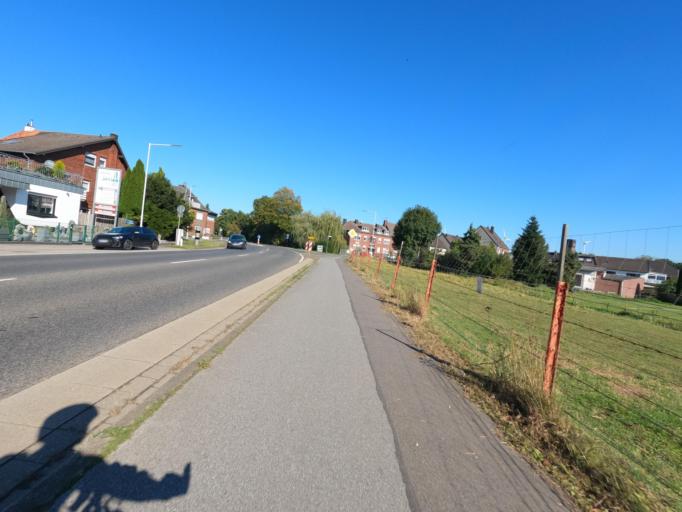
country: DE
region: North Rhine-Westphalia
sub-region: Regierungsbezirk Koln
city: Linnich
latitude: 50.9986
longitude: 6.2758
